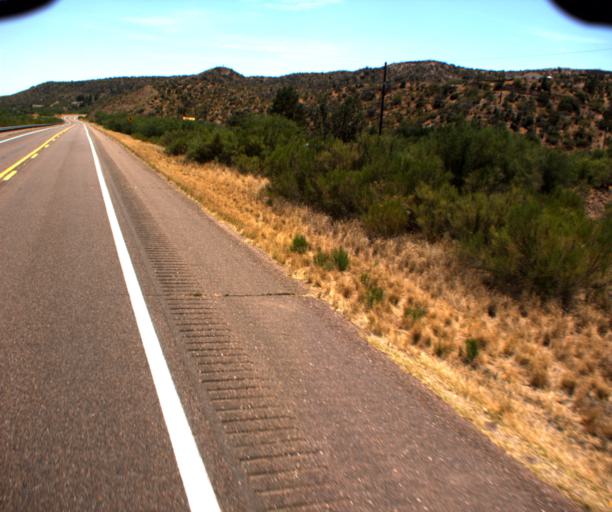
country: US
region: Arizona
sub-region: Gila County
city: Tonto Basin
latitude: 33.9572
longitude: -111.3251
